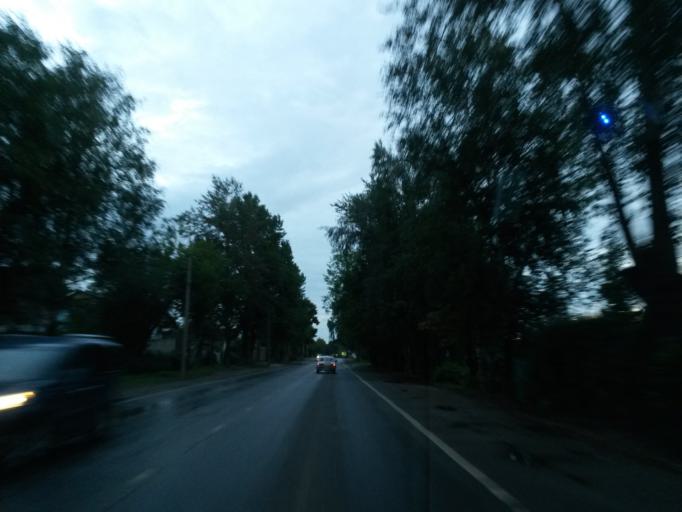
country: RU
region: Jaroslavl
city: Yaroslavl
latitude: 57.6635
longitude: 39.9093
